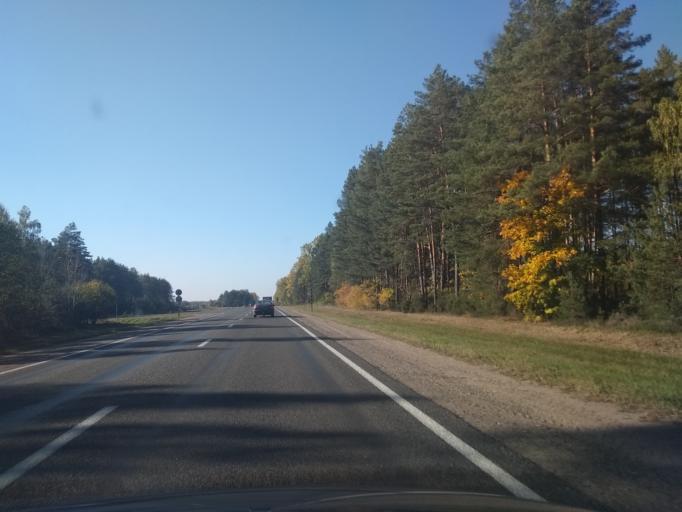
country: BY
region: Grodnenskaya
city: Zhyrovichy
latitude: 53.0629
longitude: 25.4172
